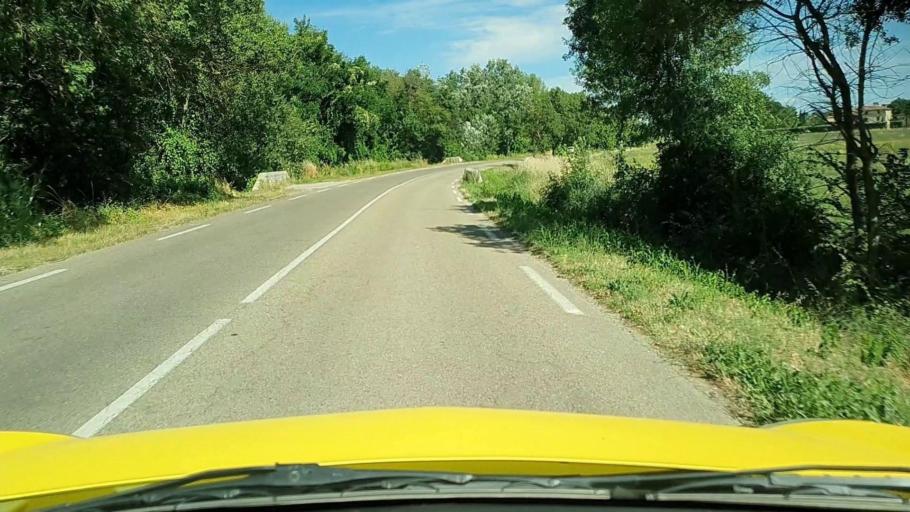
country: FR
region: Languedoc-Roussillon
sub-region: Departement du Gard
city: Saint-Hilaire-de-Brethmas
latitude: 44.0778
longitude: 4.1150
